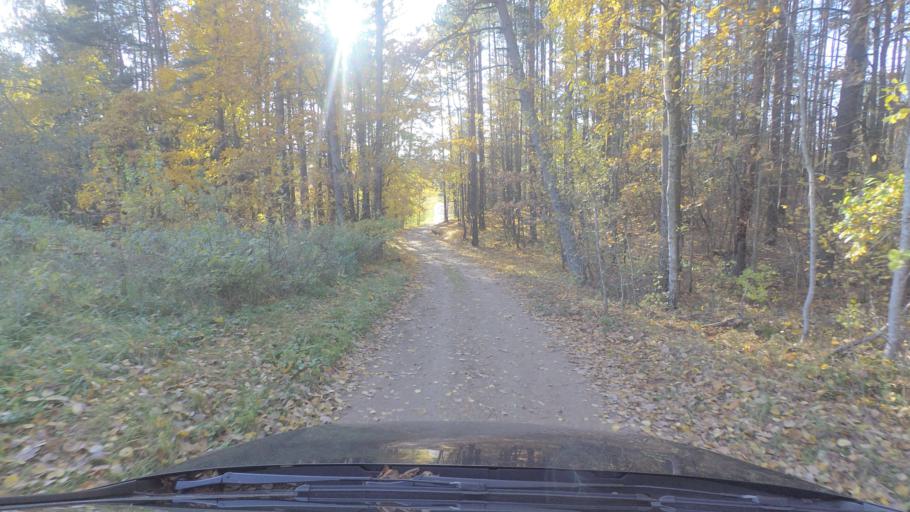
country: LT
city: Ignalina
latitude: 55.3367
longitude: 26.1766
